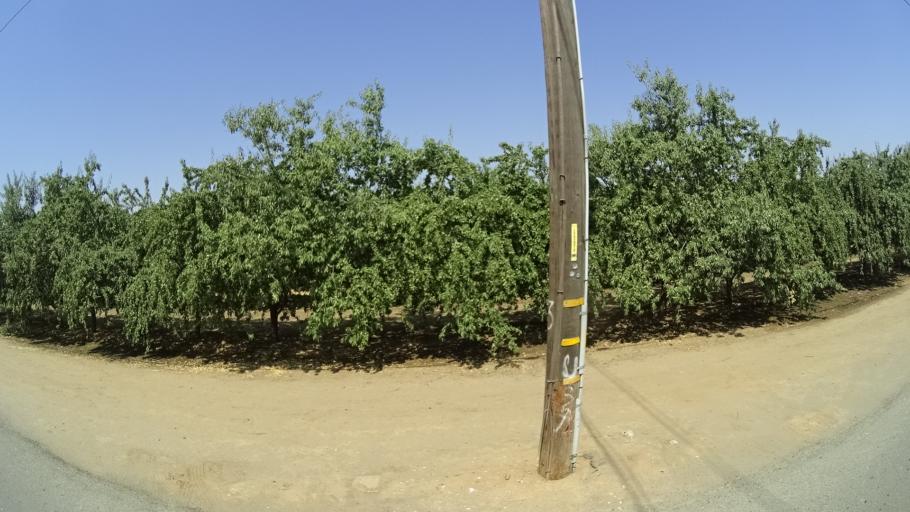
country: US
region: California
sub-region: Fresno County
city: West Park
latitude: 36.7334
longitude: -119.8534
